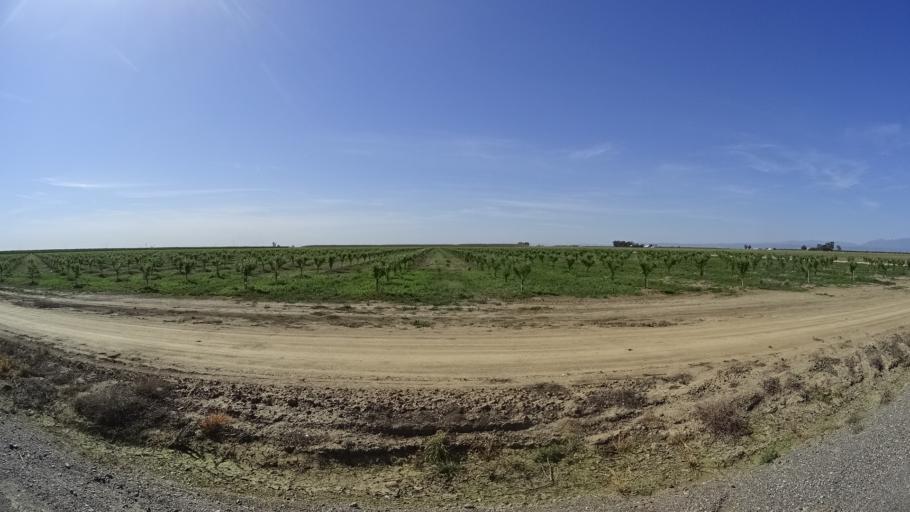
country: US
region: California
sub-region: Glenn County
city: Willows
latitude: 39.6238
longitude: -122.1431
